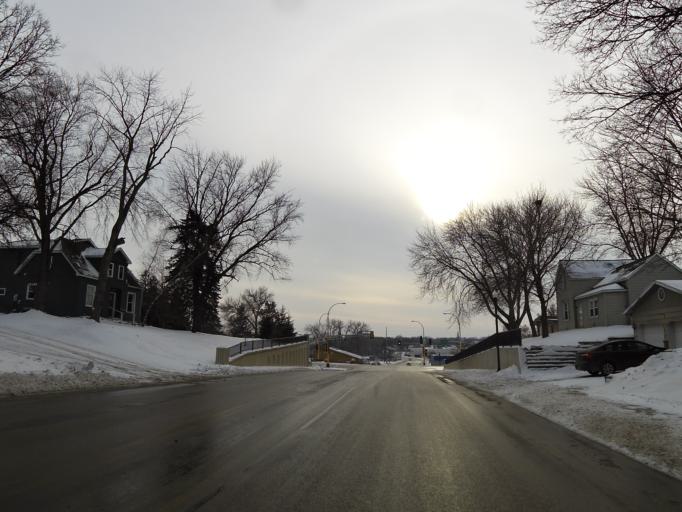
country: US
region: Minnesota
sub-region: McLeod County
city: Hutchinson
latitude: 44.8962
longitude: -94.3623
